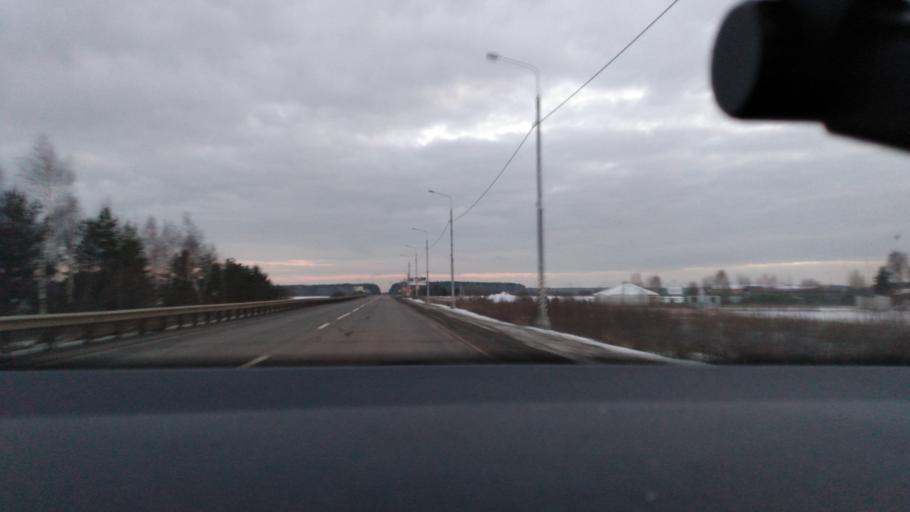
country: RU
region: Moskovskaya
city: Yegor'yevsk
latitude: 55.4418
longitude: 39.0181
